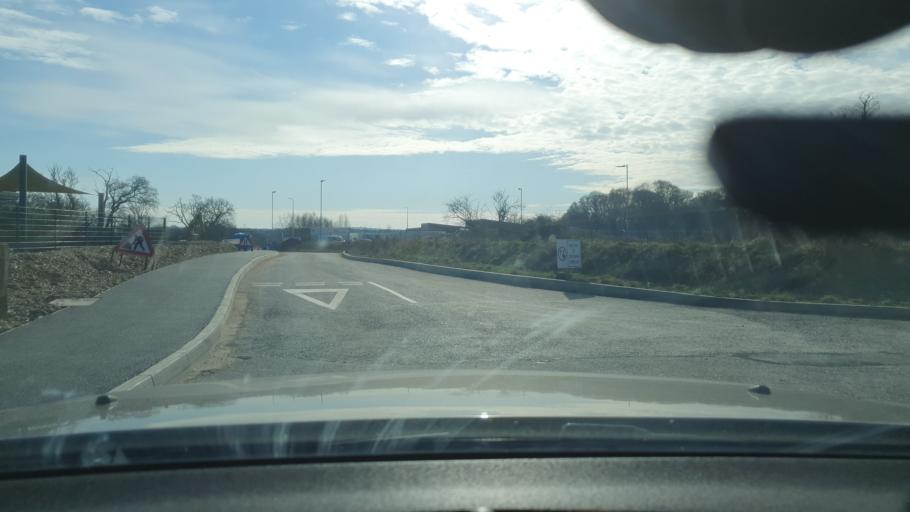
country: GB
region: England
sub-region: West Berkshire
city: Greenham
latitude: 51.3818
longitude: -1.3219
